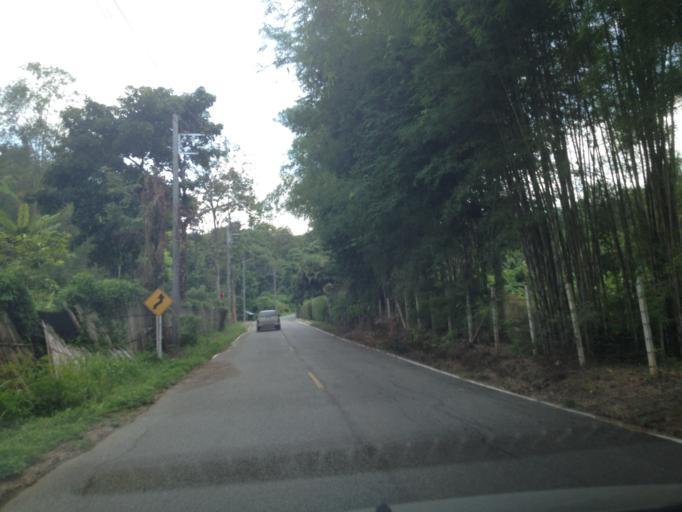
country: TH
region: Chiang Mai
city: Hang Dong
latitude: 18.7542
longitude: 98.9011
